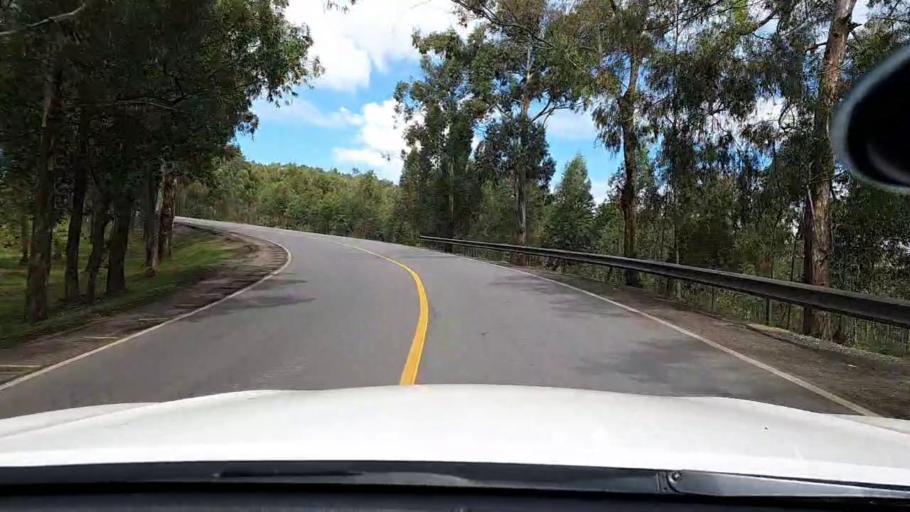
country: RW
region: Kigali
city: Kigali
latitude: -1.8165
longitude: 29.9413
